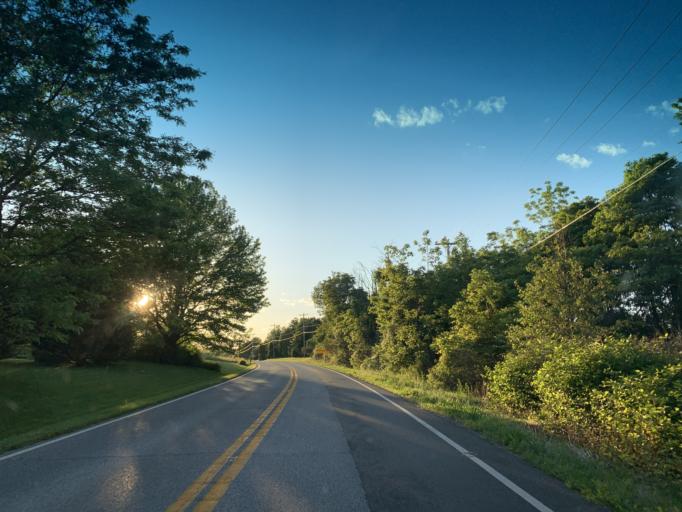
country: US
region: Maryland
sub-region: Cecil County
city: Elkton
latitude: 39.7126
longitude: -75.8707
